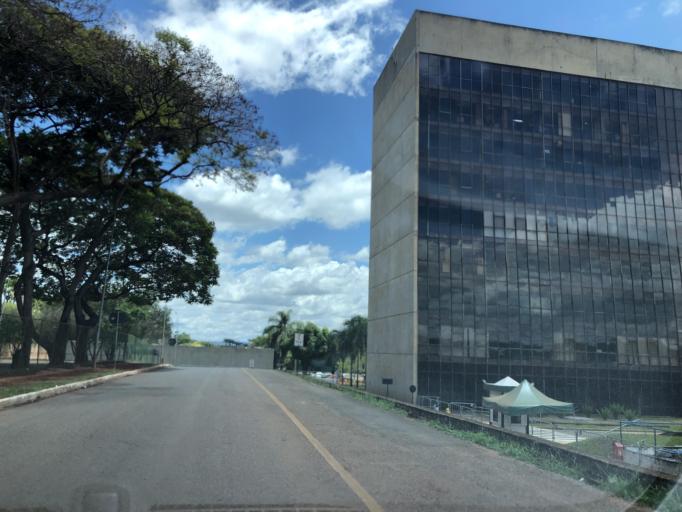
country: BR
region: Federal District
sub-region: Brasilia
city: Brasilia
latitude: -15.8028
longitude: -47.8667
